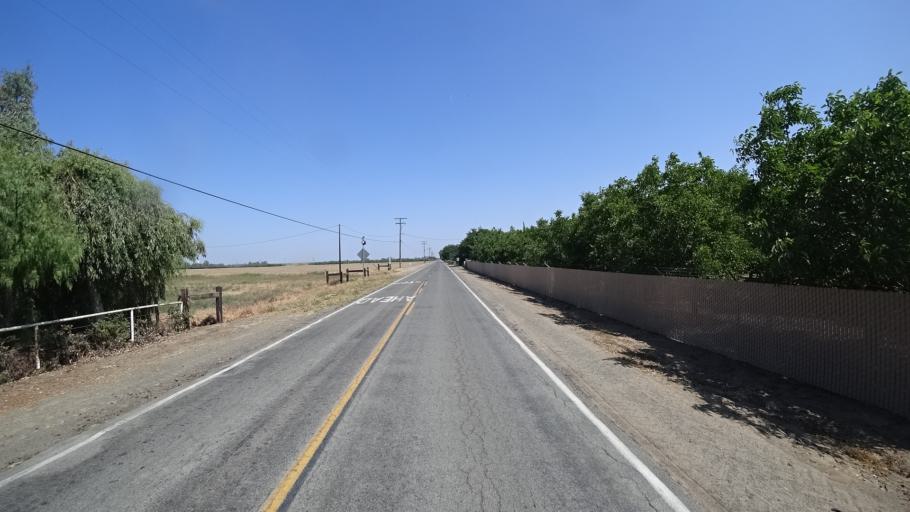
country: US
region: California
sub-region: Kings County
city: Home Garden
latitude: 36.2992
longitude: -119.6190
